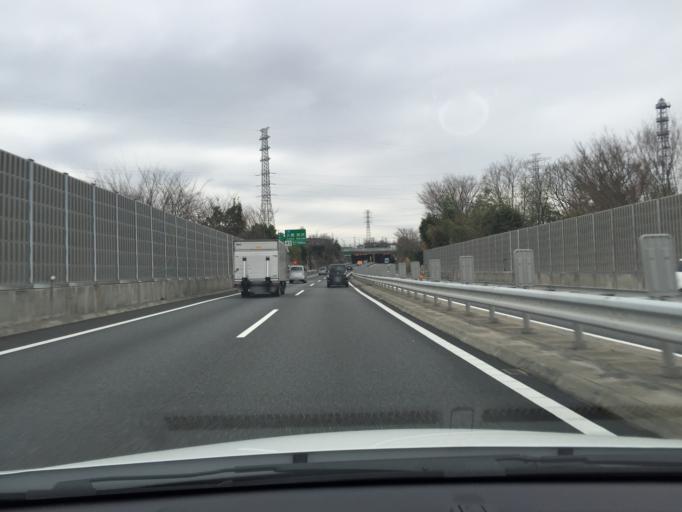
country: JP
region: Saitama
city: Sayama
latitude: 35.8250
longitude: 139.3736
